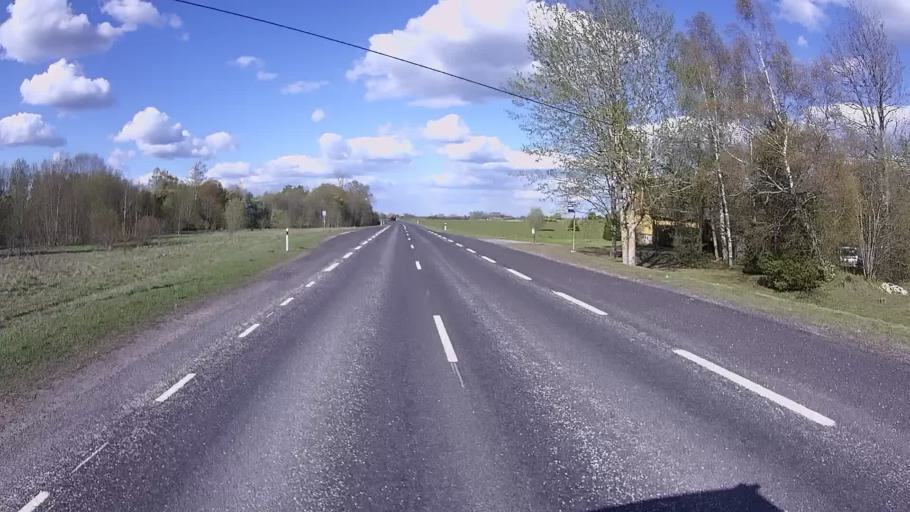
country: EE
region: Jogevamaa
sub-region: Jogeva linn
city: Jogeva
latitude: 58.7177
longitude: 26.1840
